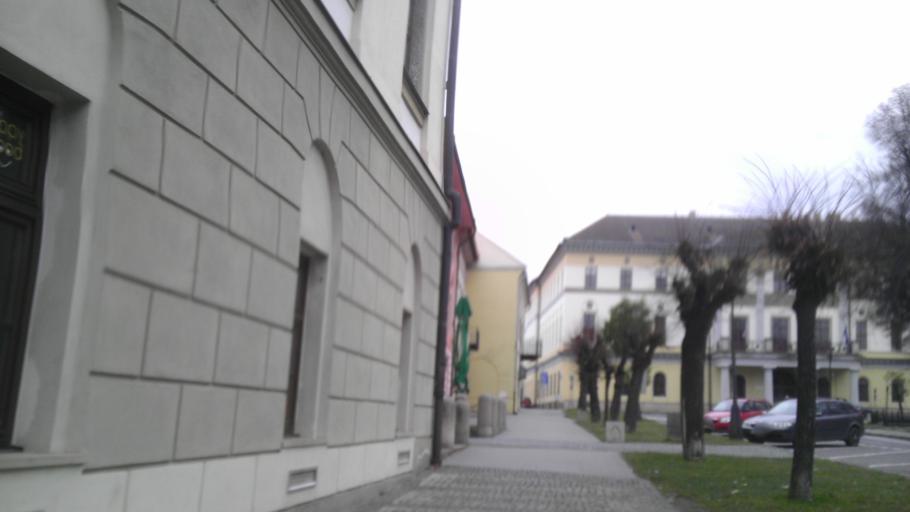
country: SK
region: Presovsky
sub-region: Okres Presov
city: Levoca
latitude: 49.0271
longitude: 20.5891
